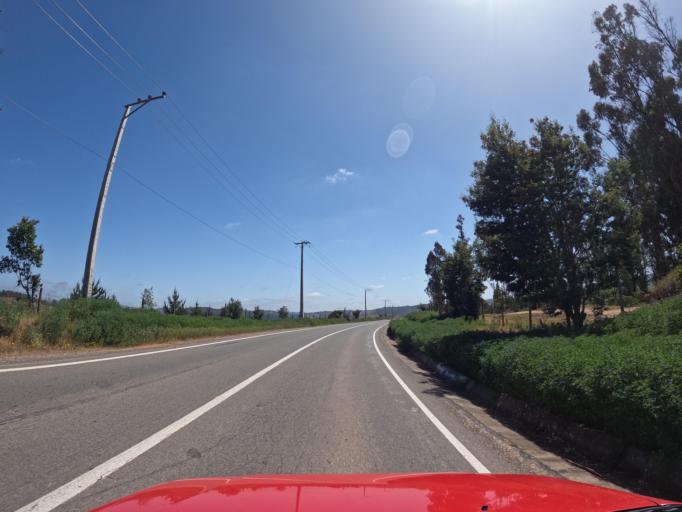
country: CL
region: O'Higgins
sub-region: Provincia de Colchagua
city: Santa Cruz
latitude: -34.6585
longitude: -71.8574
